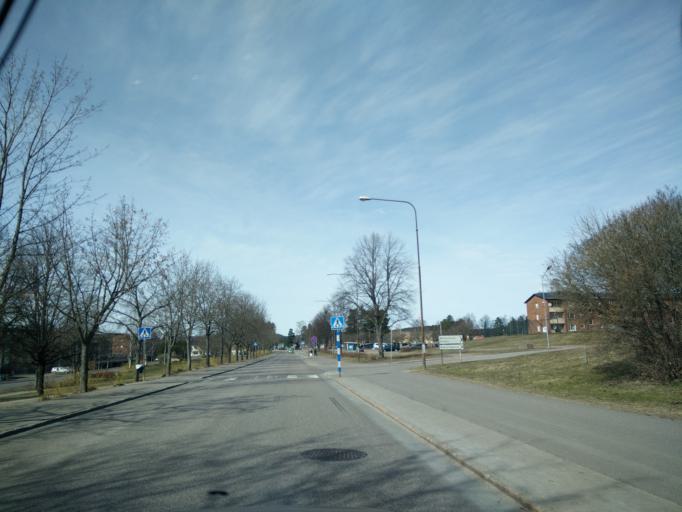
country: SE
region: Vaermland
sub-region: Hagfors Kommun
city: Hagfors
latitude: 60.0378
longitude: 13.6927
